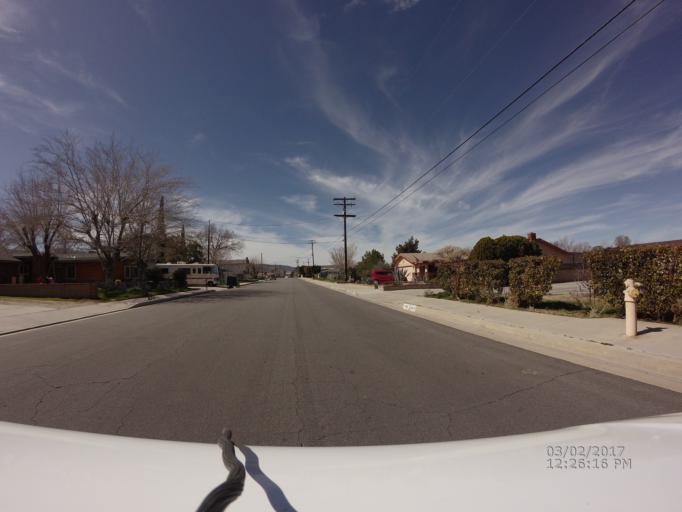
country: US
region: California
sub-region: Los Angeles County
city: Quartz Hill
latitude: 34.6493
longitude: -118.2160
